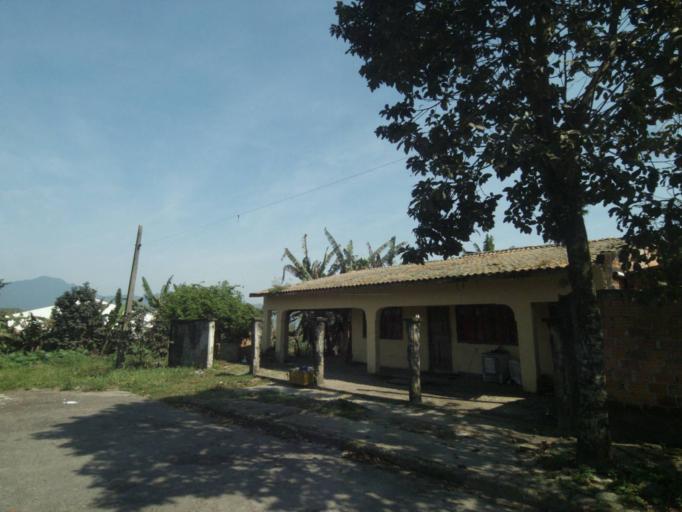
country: BR
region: Parana
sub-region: Paranagua
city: Paranagua
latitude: -25.5515
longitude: -48.5557
